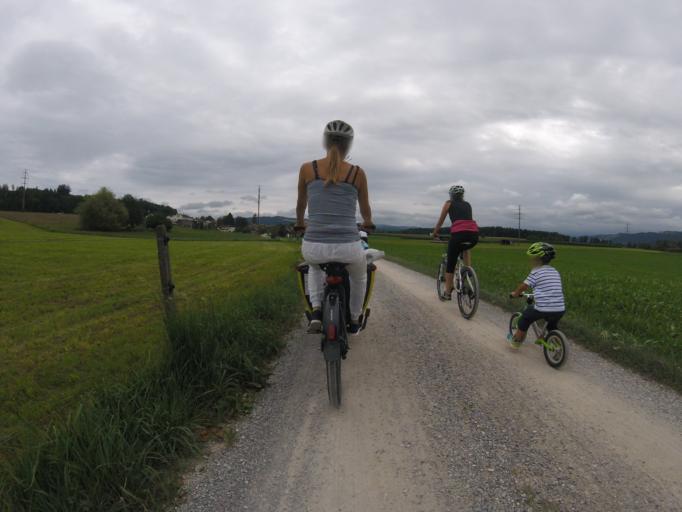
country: CH
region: Bern
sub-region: Bern-Mittelland District
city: Rubigen
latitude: 46.9187
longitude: 7.5393
